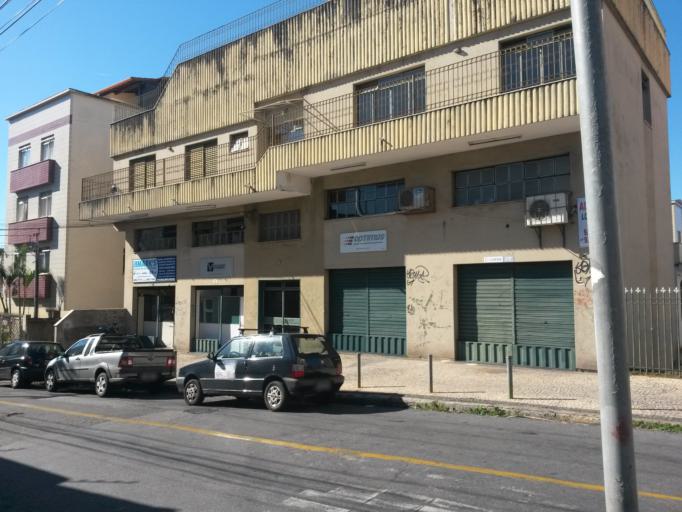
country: BR
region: Minas Gerais
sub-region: Belo Horizonte
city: Belo Horizonte
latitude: -19.9104
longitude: -43.9774
